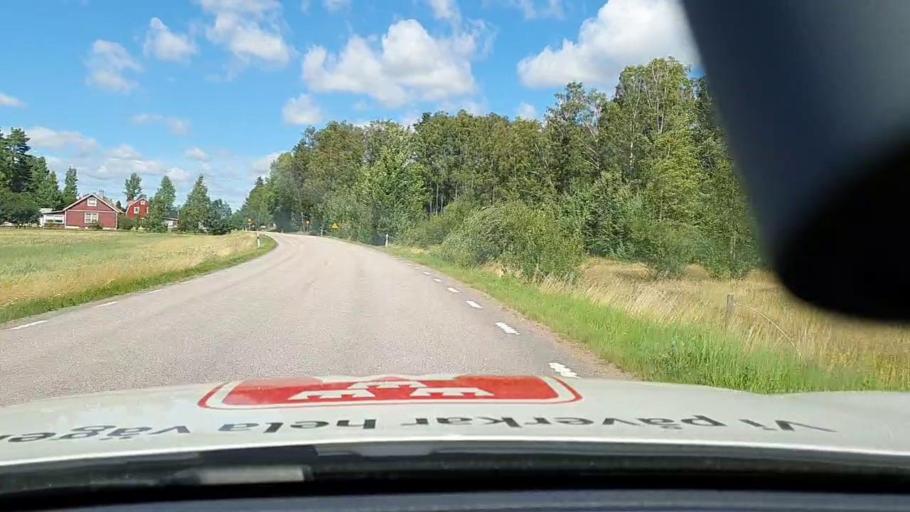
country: SE
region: Vaestra Goetaland
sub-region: Skovde Kommun
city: Stopen
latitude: 58.4998
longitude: 13.9698
